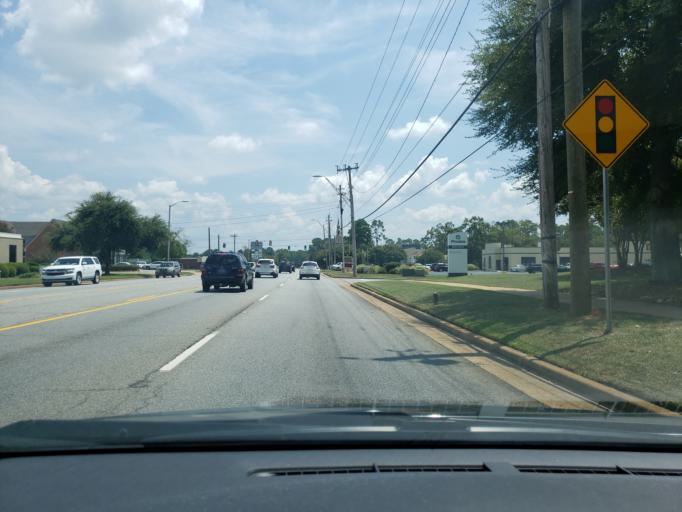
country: US
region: Georgia
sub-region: Dougherty County
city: Albany
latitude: 31.6044
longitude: -84.2055
